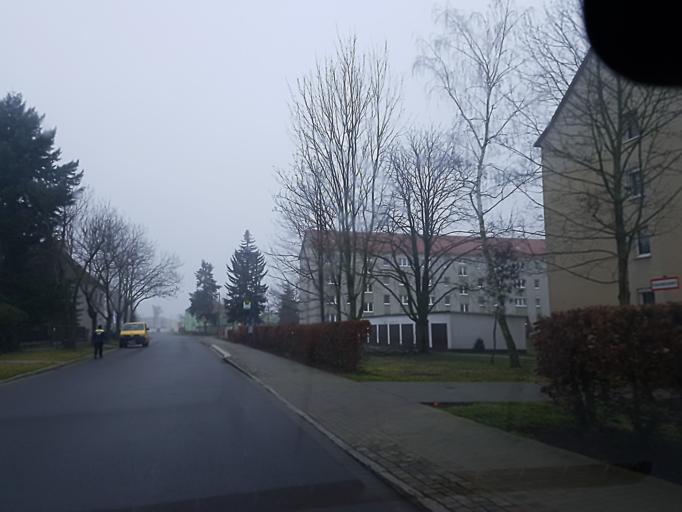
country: DE
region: Brandenburg
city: Finsterwalde
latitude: 51.6339
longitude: 13.7236
